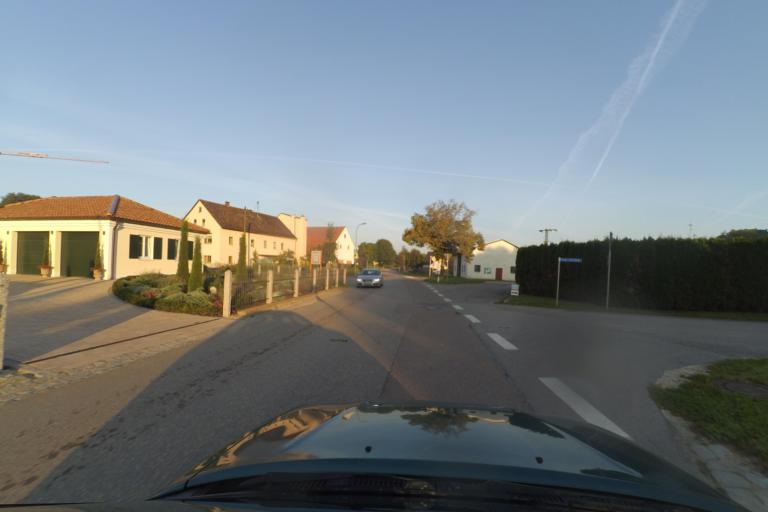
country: DE
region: Bavaria
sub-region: Lower Bavaria
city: Aiglsbach
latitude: 48.6688
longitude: 11.7209
